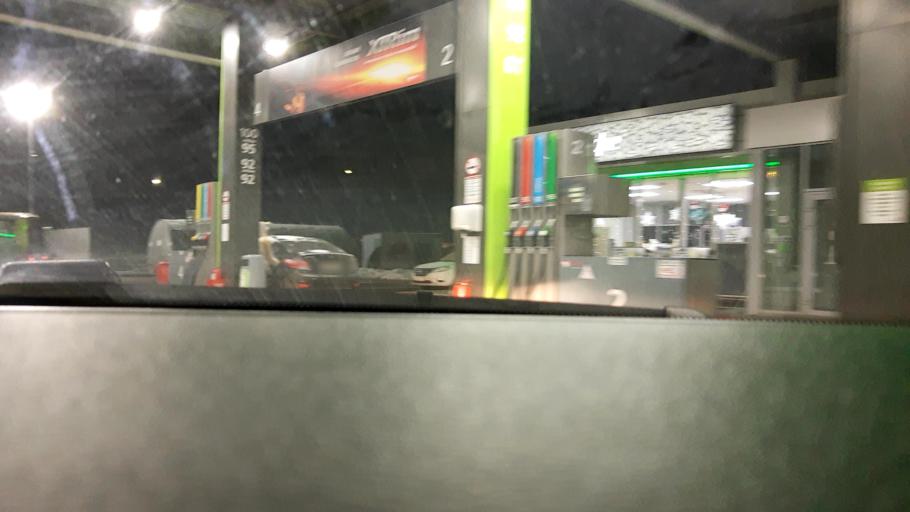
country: RU
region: Nizjnij Novgorod
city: Afonino
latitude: 56.2185
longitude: 44.1048
